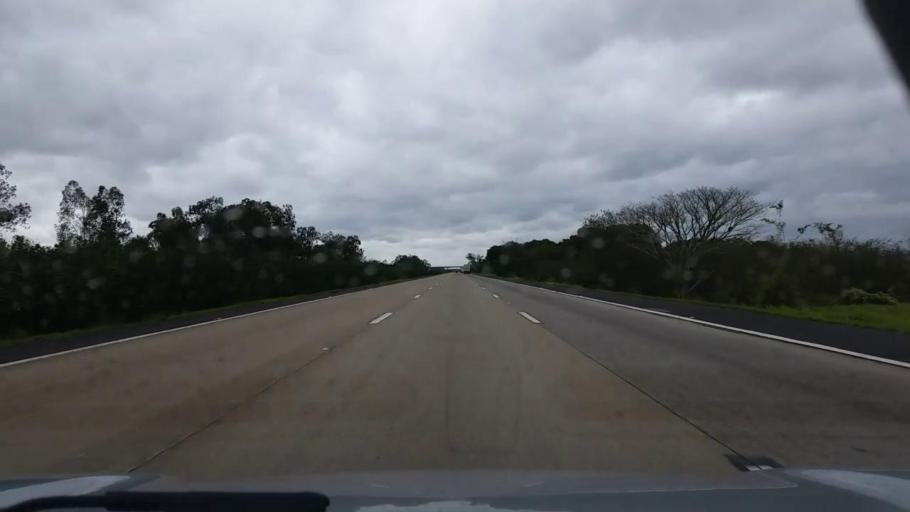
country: BR
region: Rio Grande do Sul
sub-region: Rolante
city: Rolante
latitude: -29.8863
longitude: -50.6455
